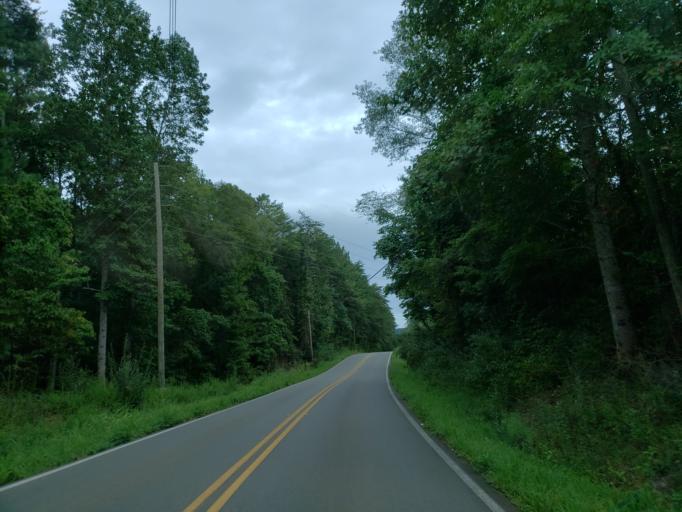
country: US
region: Georgia
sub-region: Pickens County
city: Jasper
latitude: 34.4213
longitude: -84.5765
